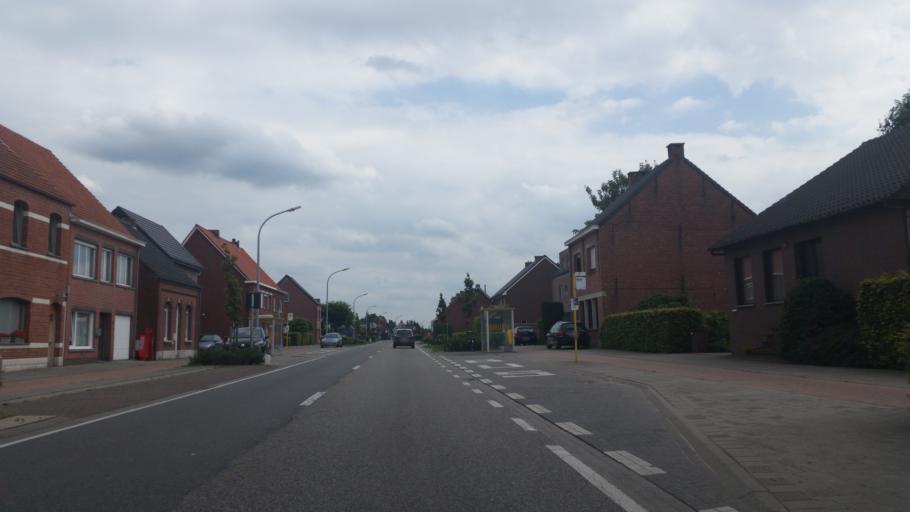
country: BE
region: Flanders
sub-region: Provincie Antwerpen
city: Merksplas
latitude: 51.3526
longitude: 4.8679
